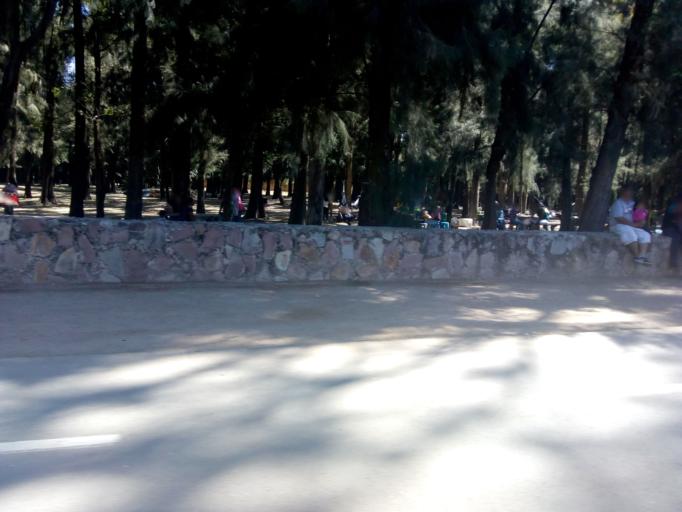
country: MX
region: Guanajuato
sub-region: Leon
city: La Ermita
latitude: 21.1727
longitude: -101.6934
